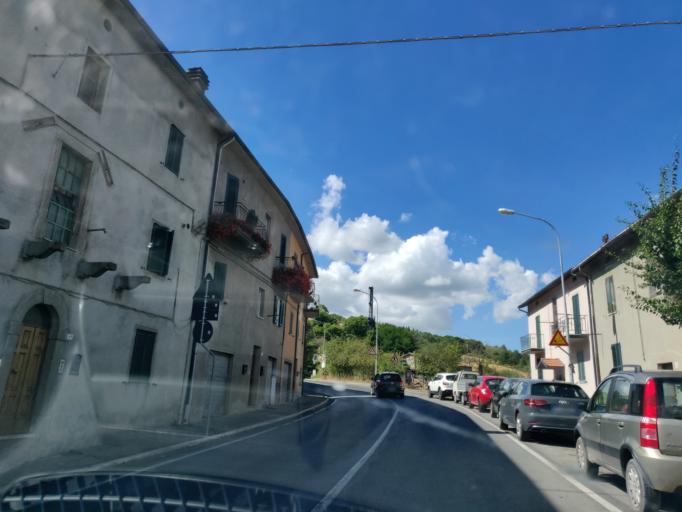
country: IT
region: Tuscany
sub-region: Provincia di Siena
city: Abbadia San Salvatore
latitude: 42.8887
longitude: 11.6668
